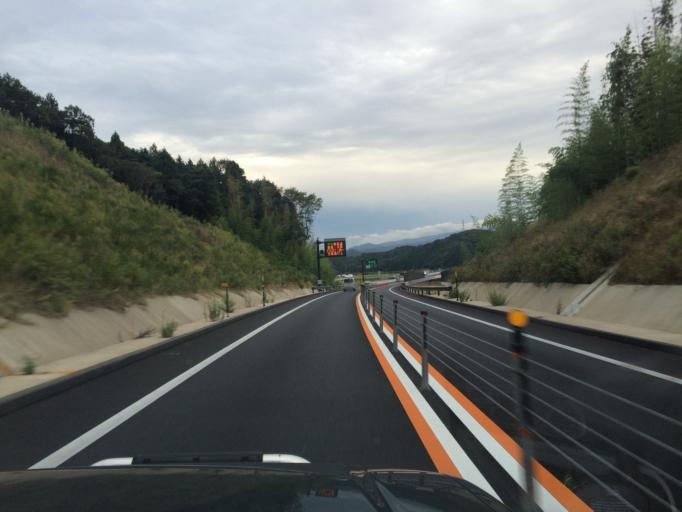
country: JP
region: Tottori
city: Tottori
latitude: 35.4952
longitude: 134.1831
